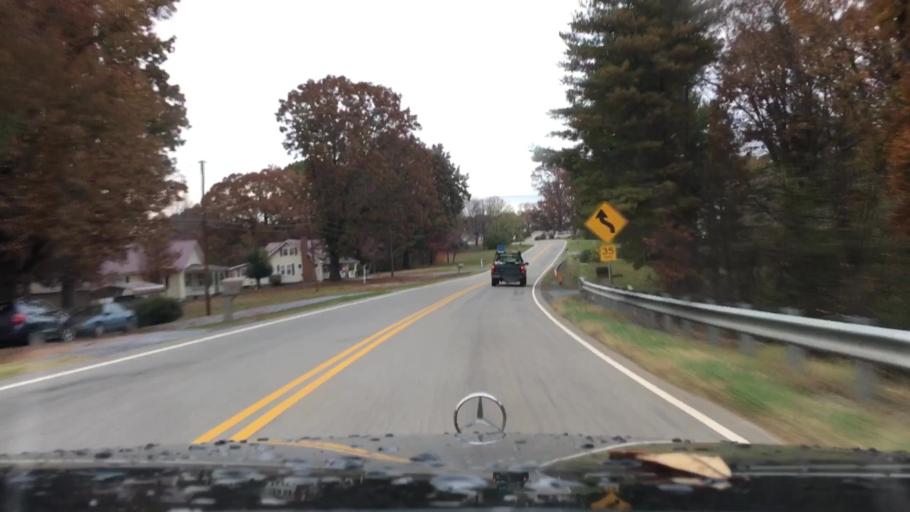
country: US
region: Virginia
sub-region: Campbell County
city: Altavista
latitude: 37.1367
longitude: -79.3067
